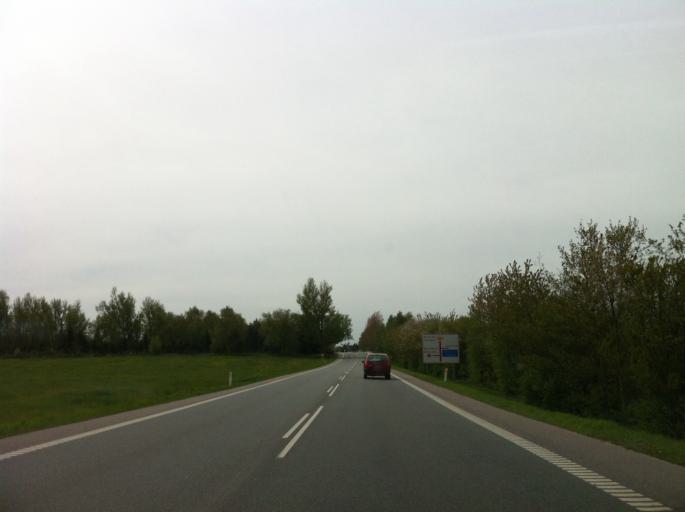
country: DK
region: Capital Region
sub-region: Egedal Kommune
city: Olstykke
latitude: 55.7736
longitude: 12.1474
